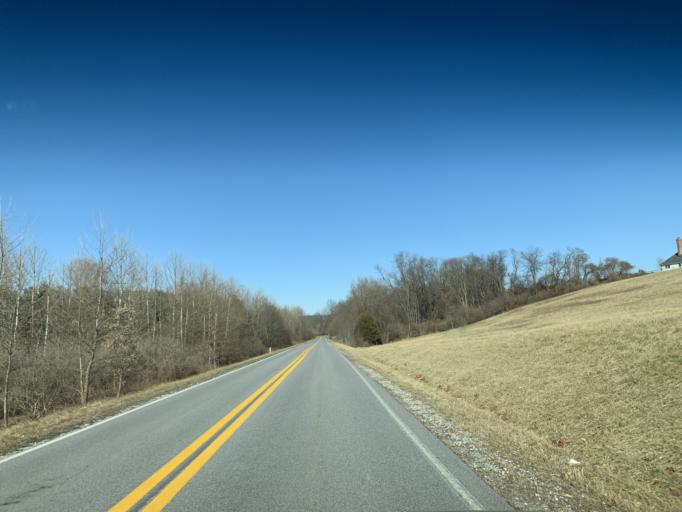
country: US
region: Maryland
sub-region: Carroll County
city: Manchester
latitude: 39.6471
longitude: -76.9620
